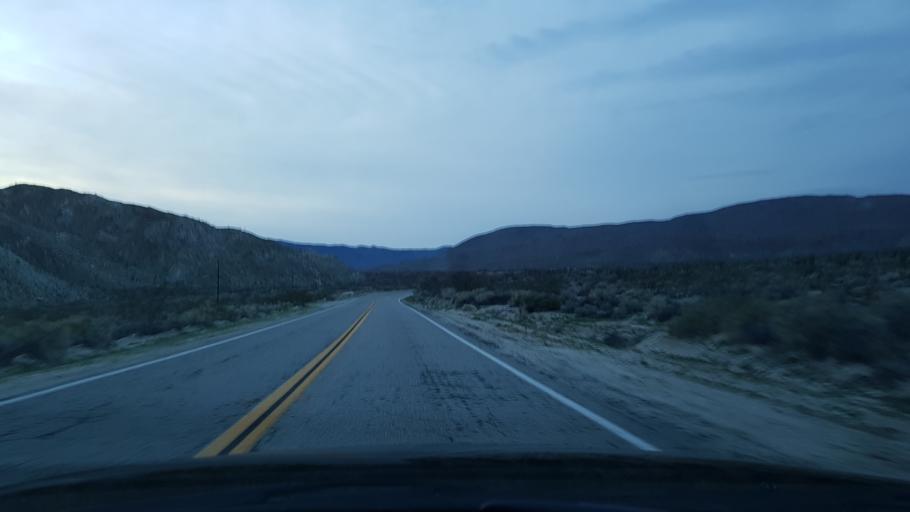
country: US
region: California
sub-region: San Diego County
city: Pine Valley
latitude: 32.9697
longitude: -116.3356
